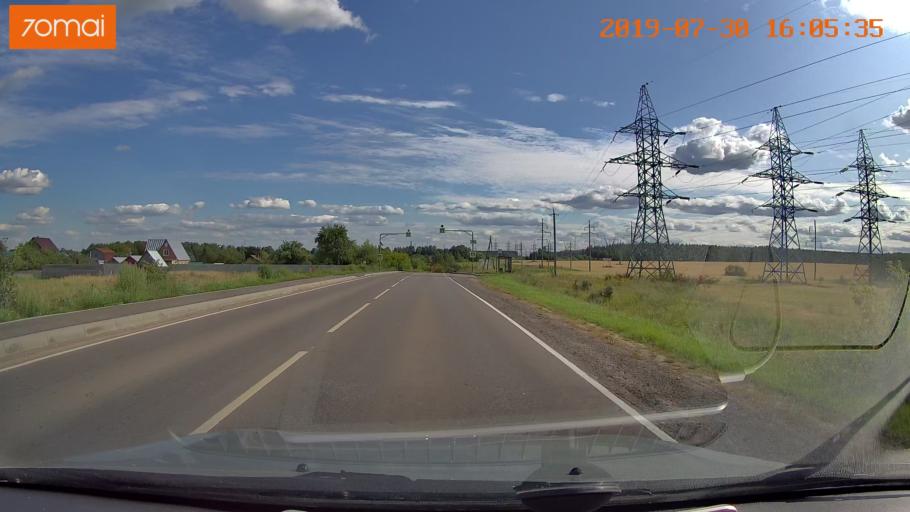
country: RU
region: Moskovskaya
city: Peski
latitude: 55.2640
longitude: 38.7154
